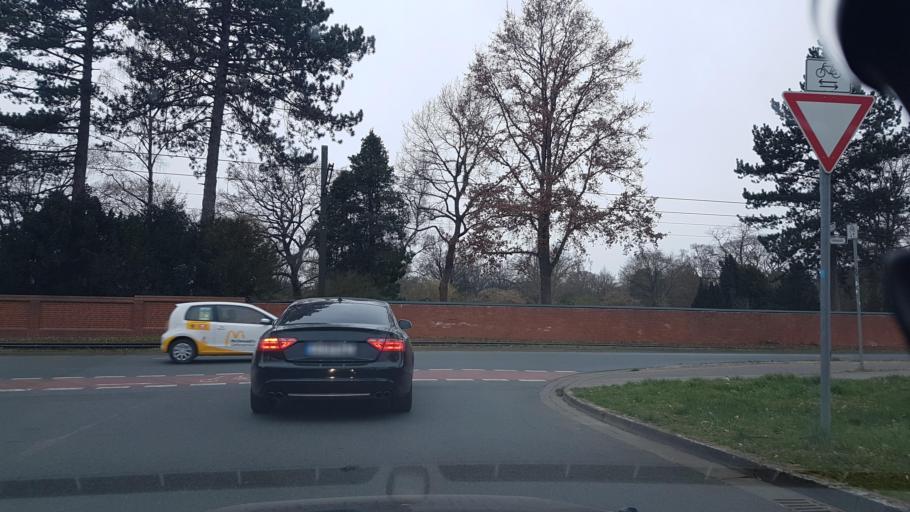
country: DE
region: Lower Saxony
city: Hannover
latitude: 52.4026
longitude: 9.6714
